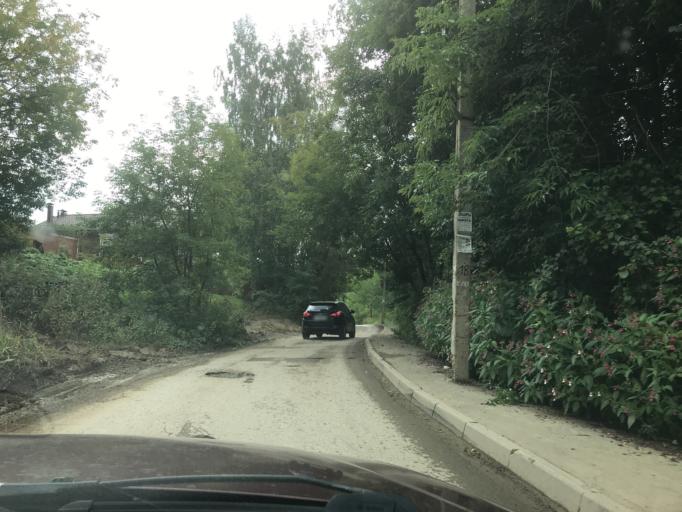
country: RU
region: Kaluga
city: Kaluga
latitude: 54.5345
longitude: 36.2406
